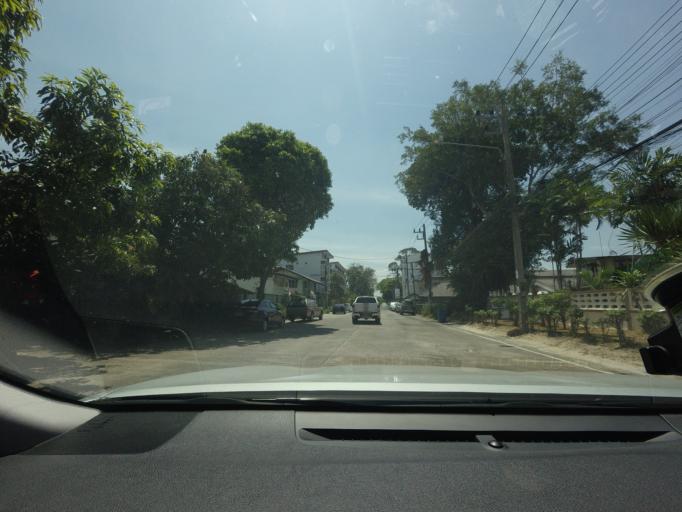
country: TH
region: Narathiwat
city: Narathiwat
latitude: 6.4257
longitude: 101.8223
